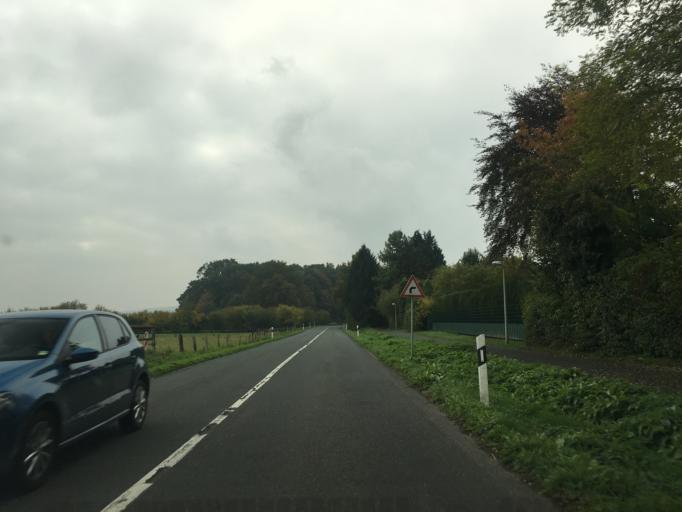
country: DE
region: North Rhine-Westphalia
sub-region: Regierungsbezirk Munster
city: Havixbeck
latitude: 51.9839
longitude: 7.4226
